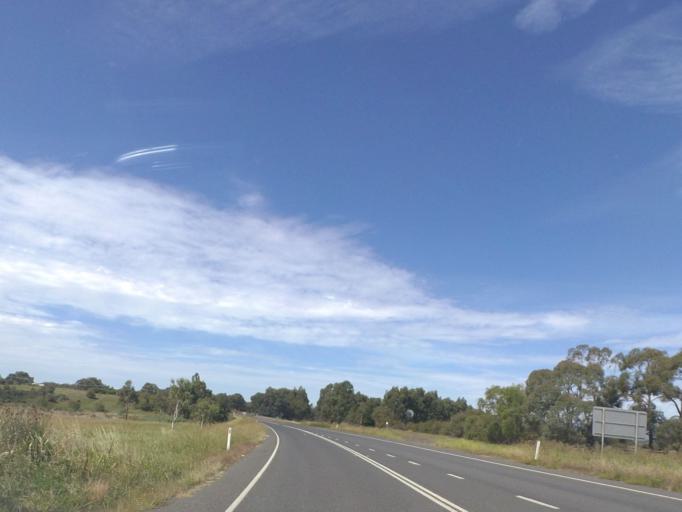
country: AU
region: Victoria
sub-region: Mount Alexander
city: Castlemaine
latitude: -37.2819
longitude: 144.4935
